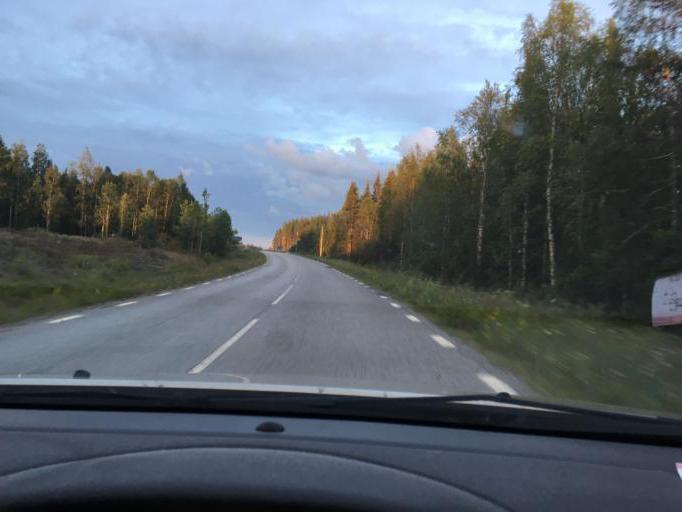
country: SE
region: Norrbotten
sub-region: Lulea Kommun
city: Ranea
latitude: 66.0431
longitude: 22.2924
